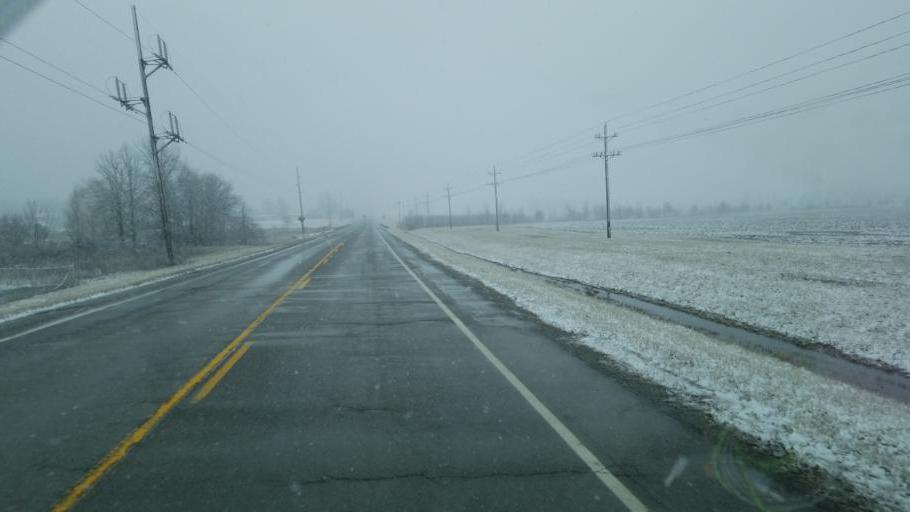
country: US
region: Ohio
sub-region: Champaign County
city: North Lewisburg
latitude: 40.3285
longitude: -83.5293
